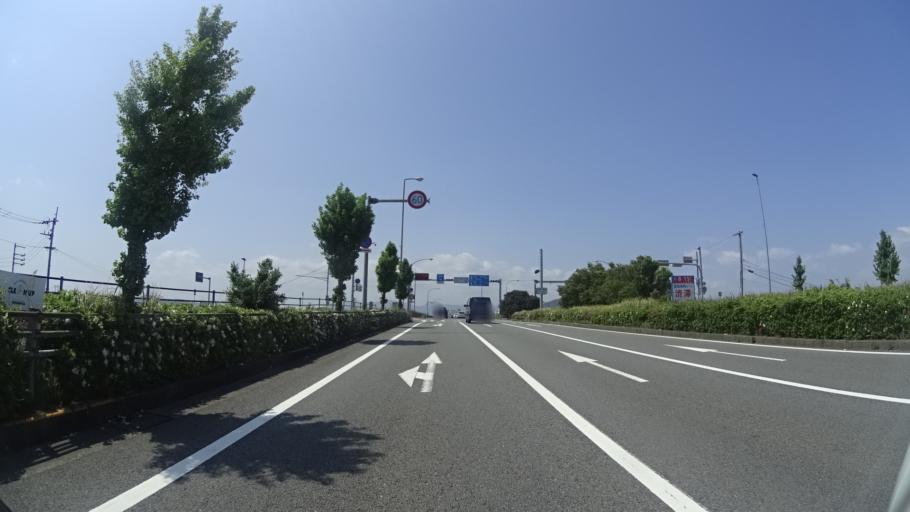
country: JP
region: Tokushima
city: Tokushima-shi
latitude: 34.0948
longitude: 134.5716
